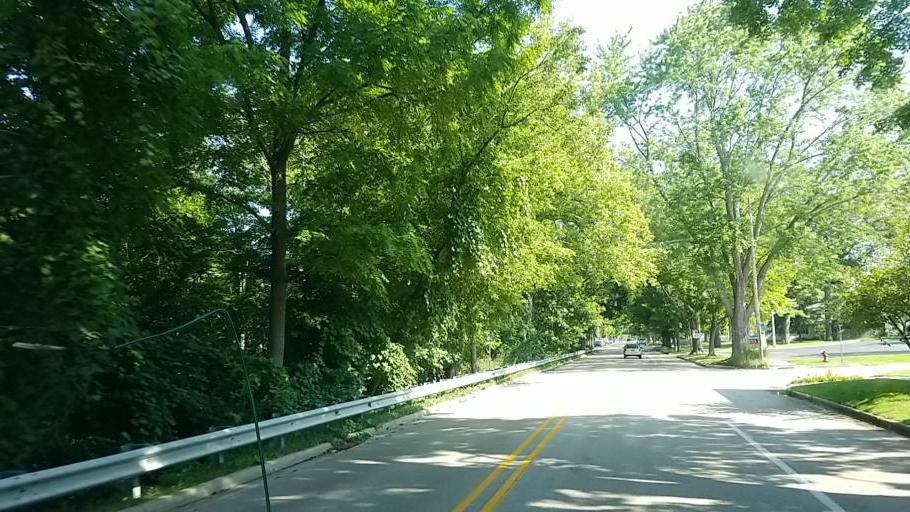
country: US
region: Michigan
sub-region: Muskegon County
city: Whitehall
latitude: 43.4045
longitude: -86.3478
